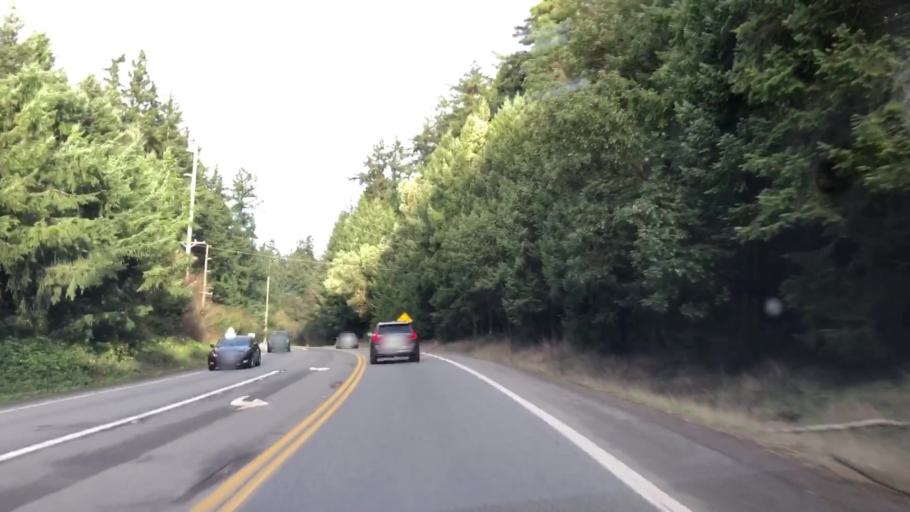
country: US
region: Washington
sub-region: Kitsap County
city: Suquamish
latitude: 47.7037
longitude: -122.5587
